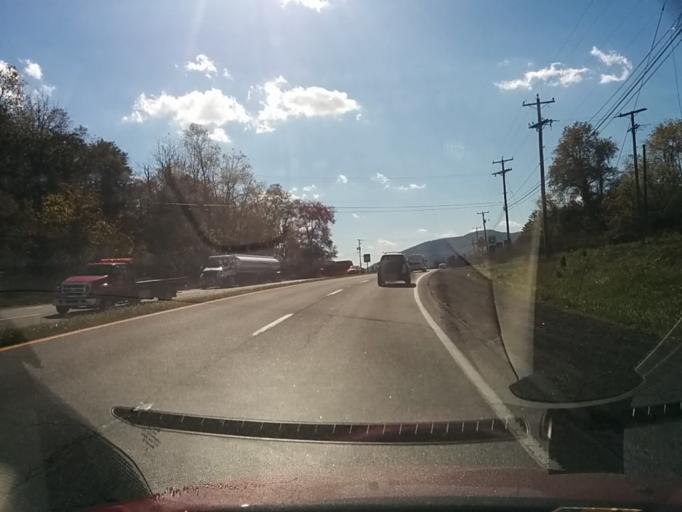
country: US
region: Virginia
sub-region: Botetourt County
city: Daleville
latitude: 37.3947
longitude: -79.9067
